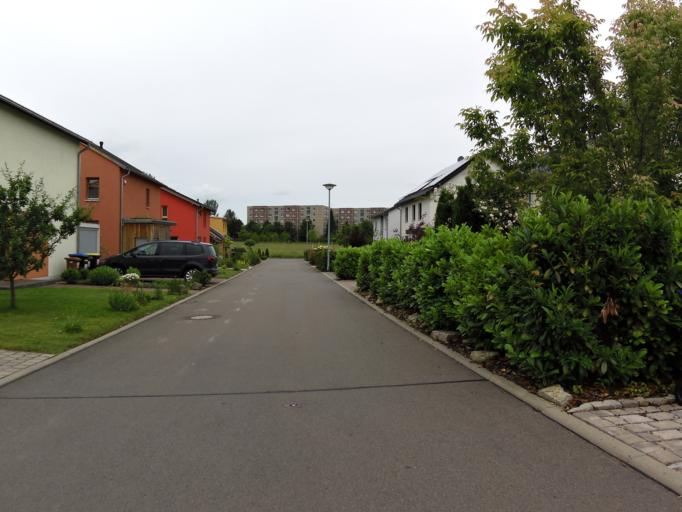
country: DE
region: Thuringia
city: Erfurt
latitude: 50.9873
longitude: 11.0109
